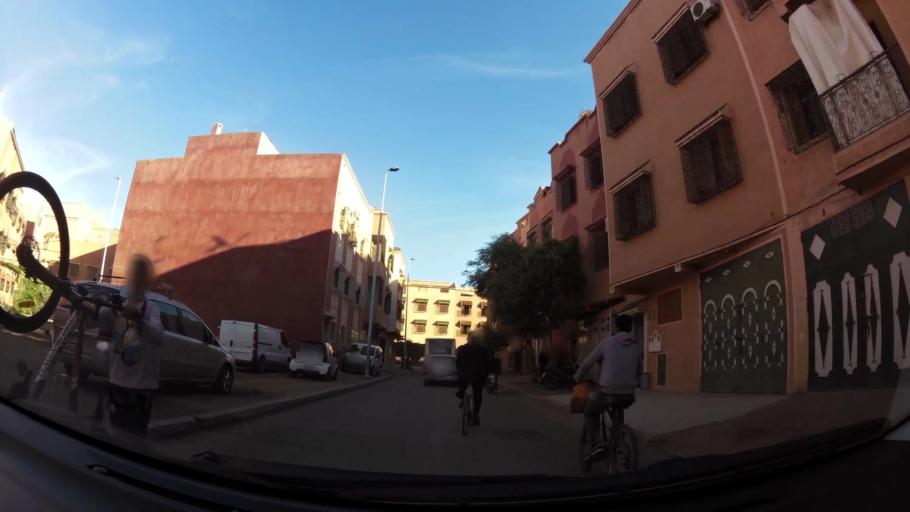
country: MA
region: Marrakech-Tensift-Al Haouz
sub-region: Marrakech
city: Marrakesh
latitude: 31.6207
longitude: -8.0658
